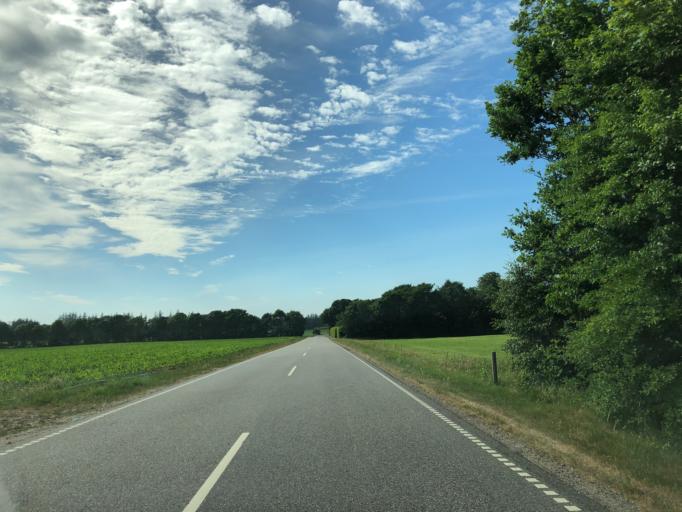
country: DK
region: Central Jutland
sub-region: Herning Kommune
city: Vildbjerg
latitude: 56.1476
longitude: 8.8018
